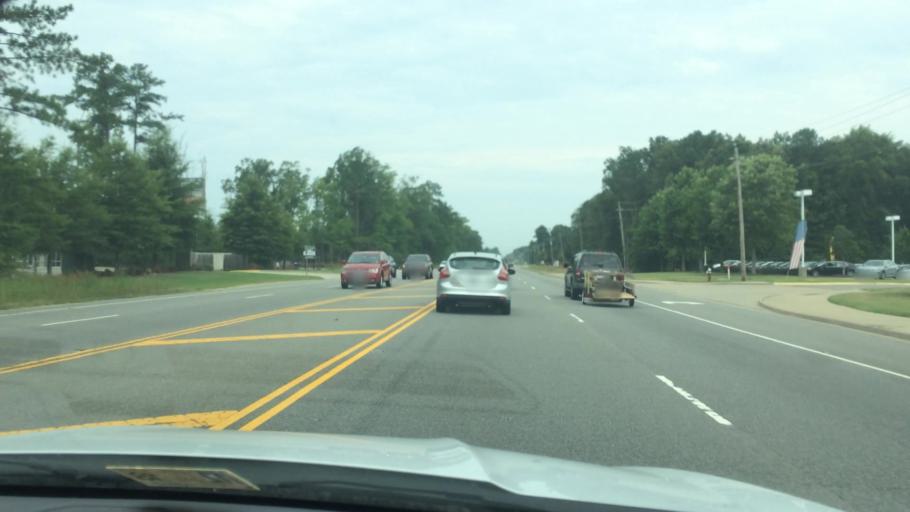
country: US
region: Virginia
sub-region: York County
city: Yorktown
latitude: 37.1583
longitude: -76.5354
